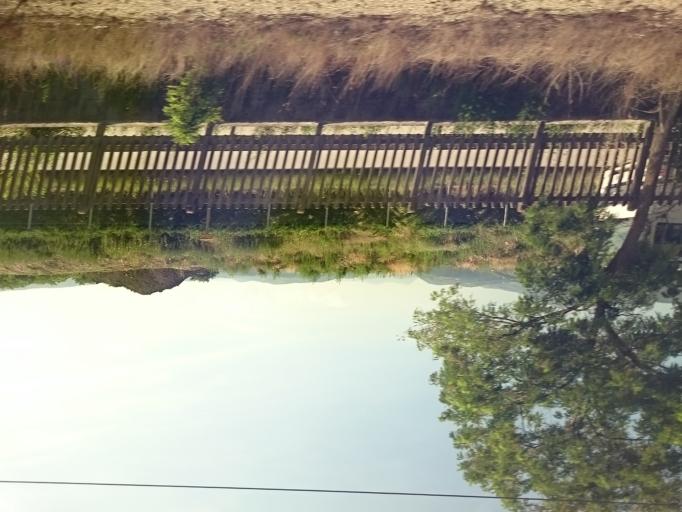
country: IT
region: Veneto
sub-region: Provincia di Verona
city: Ospedaletto
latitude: 45.5024
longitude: 10.8602
